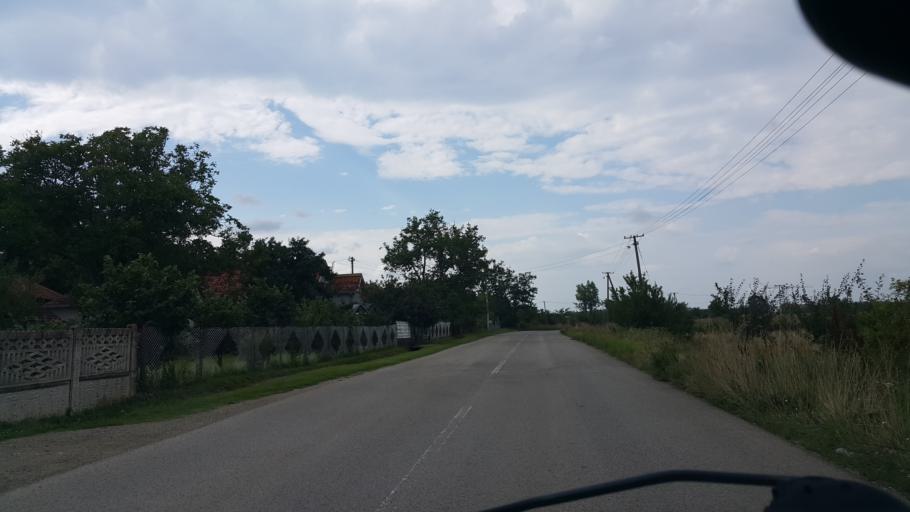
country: RS
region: Central Serbia
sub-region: Toplicki Okrug
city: Blace
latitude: 43.2328
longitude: 21.2569
